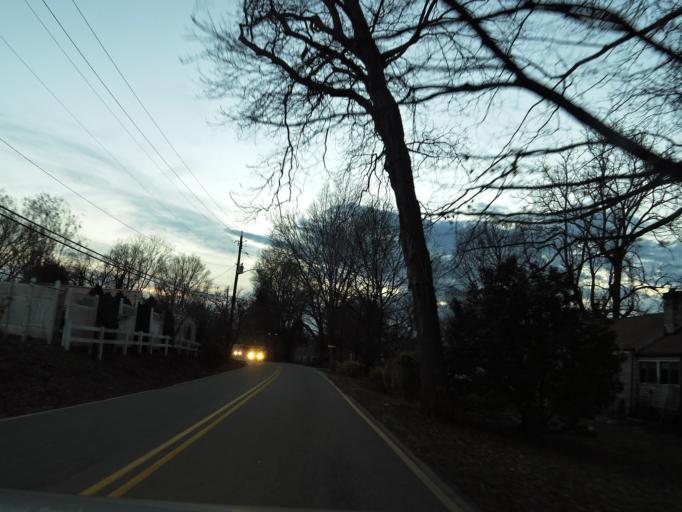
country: US
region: Tennessee
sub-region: Knox County
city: Knoxville
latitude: 35.9366
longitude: -83.8967
